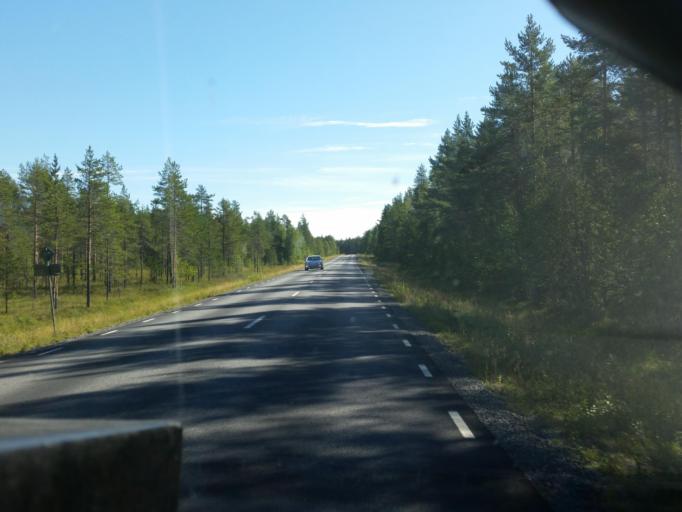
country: SE
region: Norrbotten
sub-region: Pitea Kommun
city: Roknas
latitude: 65.3423
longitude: 20.9550
